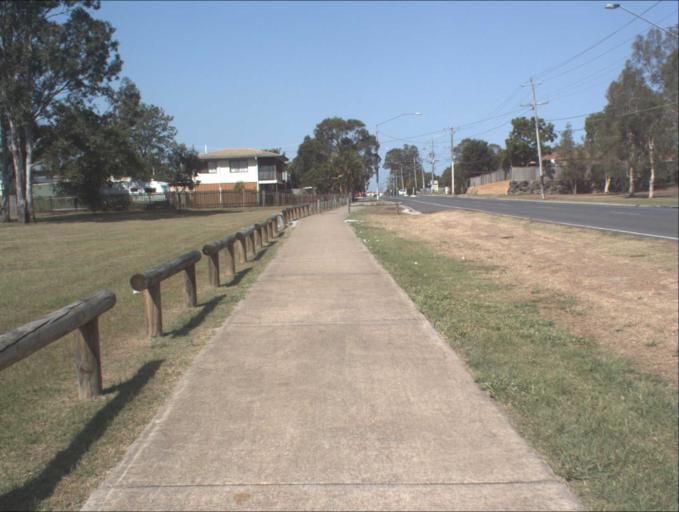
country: AU
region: Queensland
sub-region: Logan
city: Beenleigh
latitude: -27.6914
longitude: 153.1857
